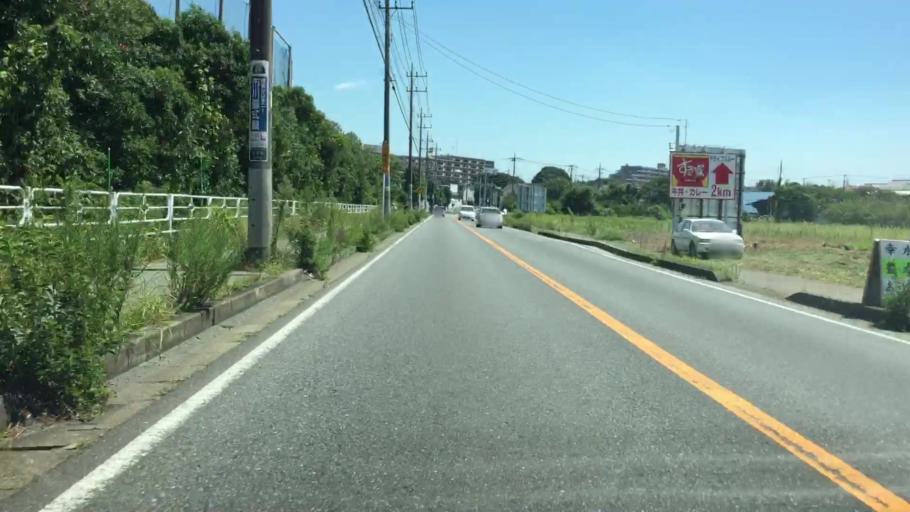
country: JP
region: Chiba
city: Funabashi
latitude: 35.7364
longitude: 139.9558
